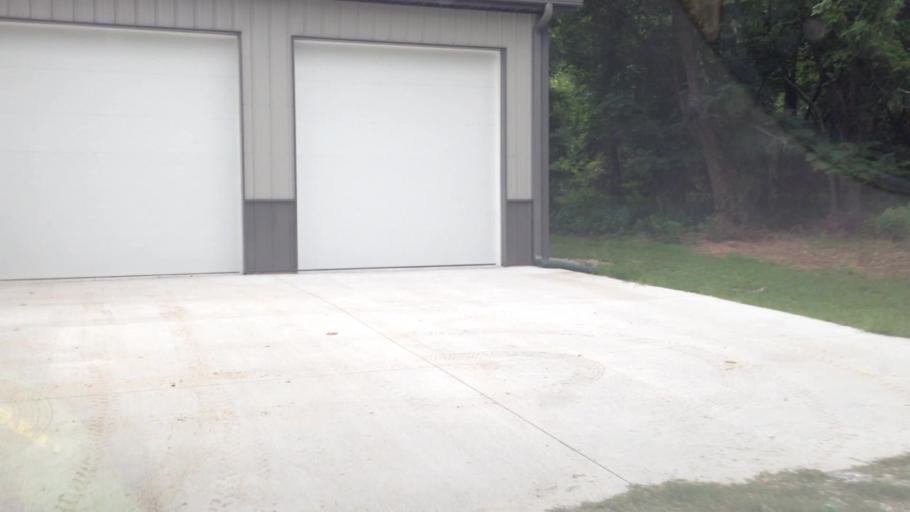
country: US
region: Oklahoma
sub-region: Delaware County
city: Cleora
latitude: 36.5493
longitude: -94.9655
